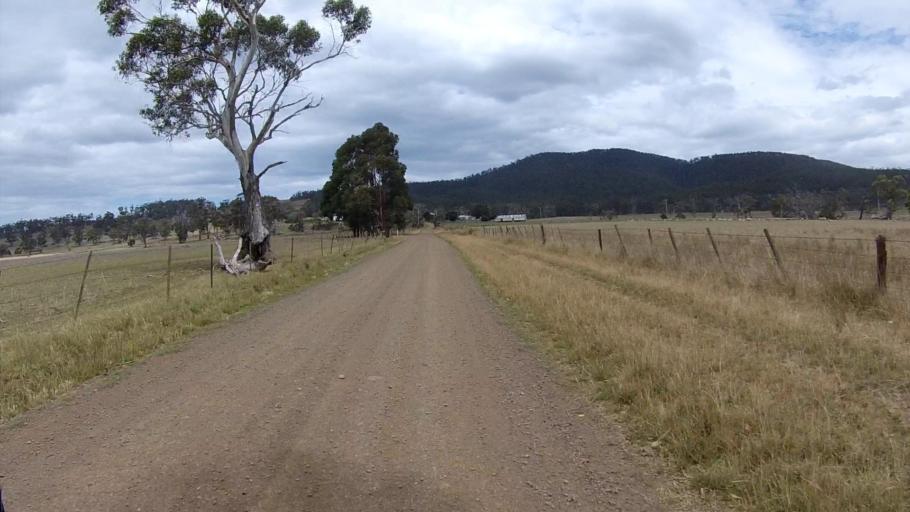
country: AU
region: Tasmania
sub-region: Sorell
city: Sorell
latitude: -42.6573
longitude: 147.9402
